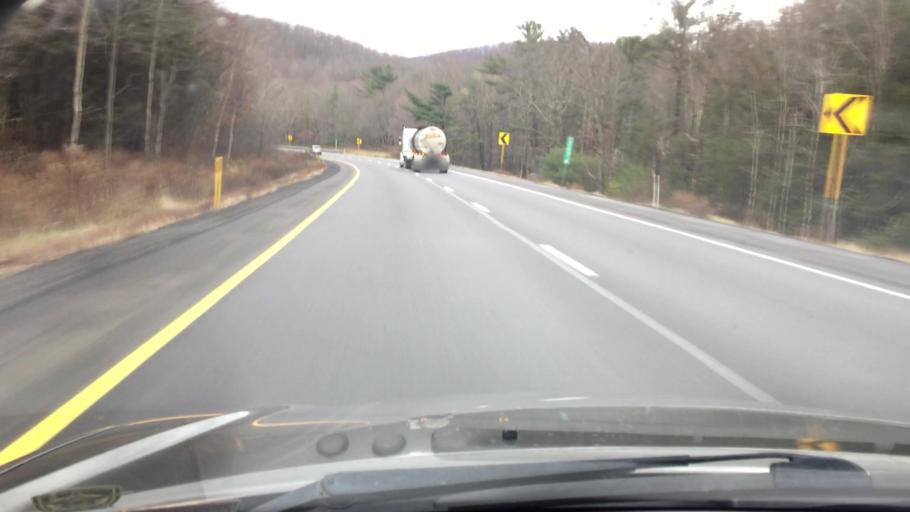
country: US
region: Pennsylvania
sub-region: Luzerne County
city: Freeland
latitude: 41.0617
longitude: -75.8654
